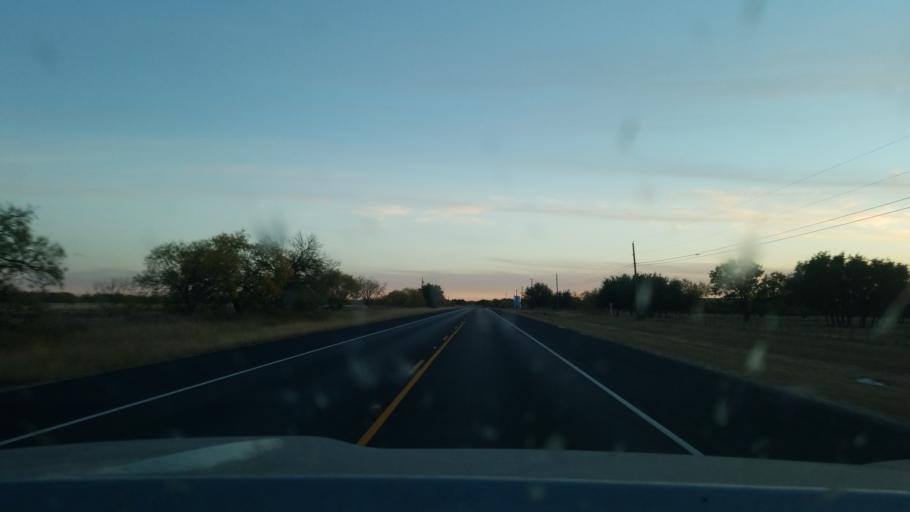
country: US
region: Texas
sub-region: Stephens County
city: Breckenridge
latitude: 32.6302
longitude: -98.9029
